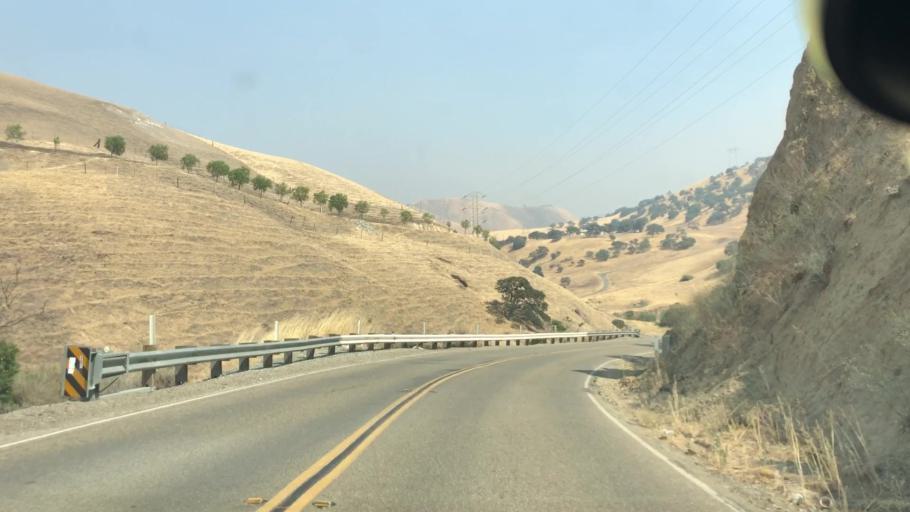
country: US
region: California
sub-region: San Joaquin County
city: Mountain House
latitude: 37.6434
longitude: -121.5965
